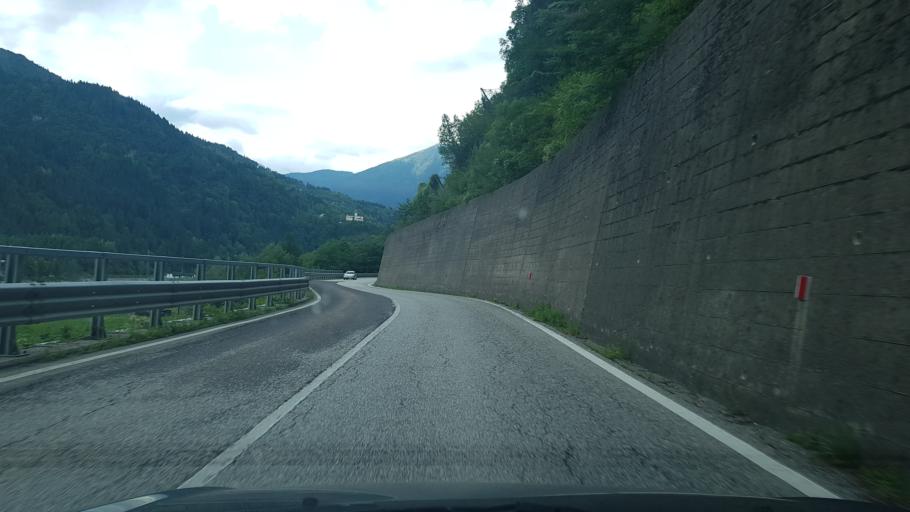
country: IT
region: Friuli Venezia Giulia
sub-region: Provincia di Udine
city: Comeglians
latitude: 46.5075
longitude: 12.8658
